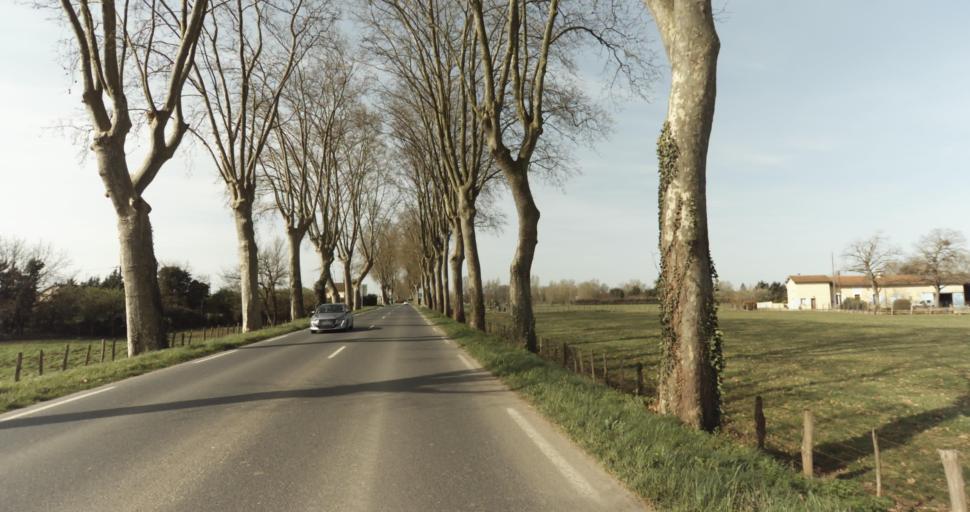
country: FR
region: Midi-Pyrenees
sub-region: Departement du Tarn
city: Saint-Sulpice-la-Pointe
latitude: 43.7726
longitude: 1.6588
